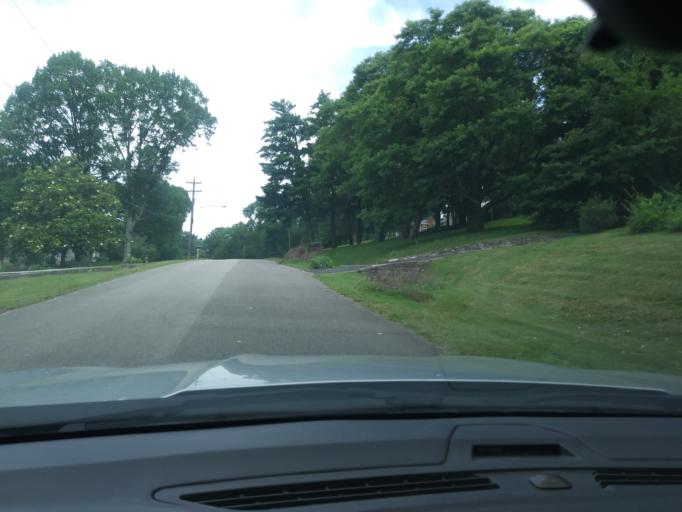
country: US
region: Tennessee
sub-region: Davidson County
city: Oak Hill
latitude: 36.1269
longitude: -86.7214
